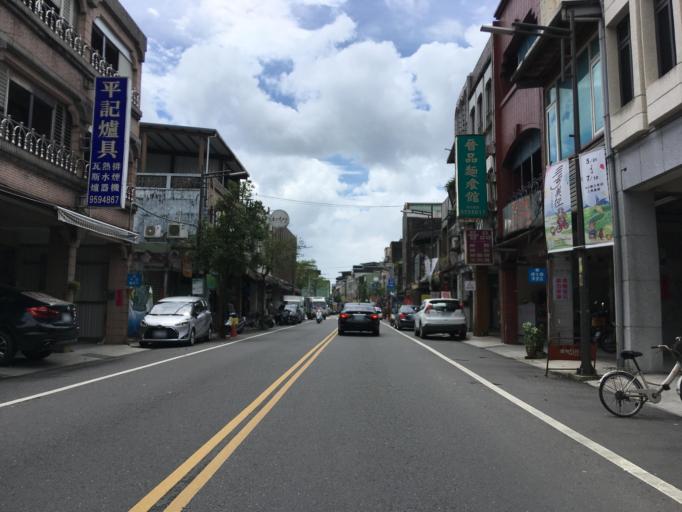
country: TW
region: Taiwan
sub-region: Yilan
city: Yilan
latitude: 24.6350
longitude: 121.7894
